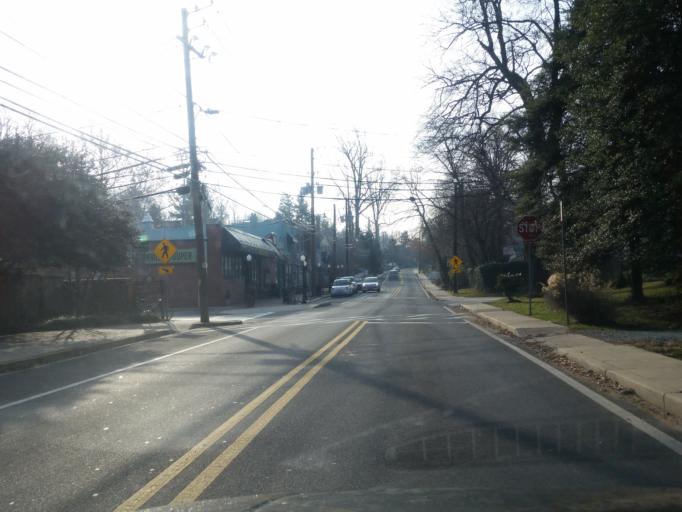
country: US
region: Maryland
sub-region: Montgomery County
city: Chevy Chase
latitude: 38.9814
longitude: -77.0716
